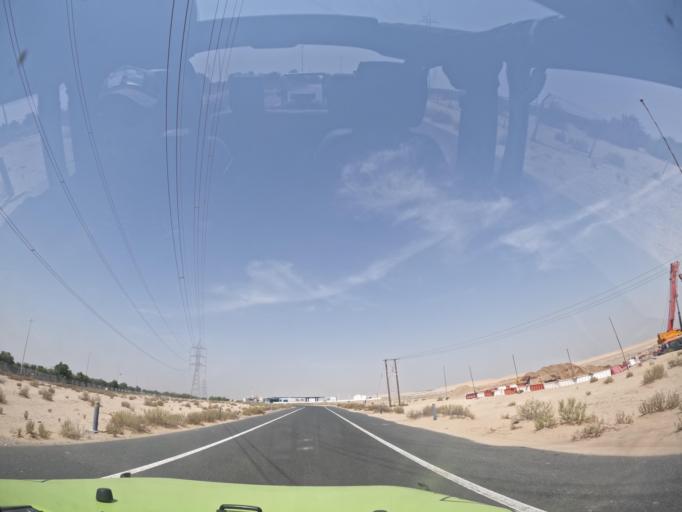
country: AE
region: Abu Dhabi
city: Abu Dhabi
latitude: 24.2186
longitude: 54.8589
